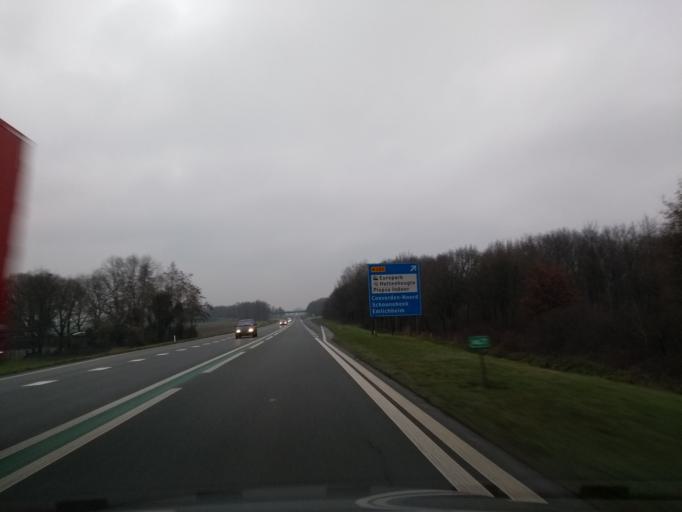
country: NL
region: Drenthe
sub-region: Gemeente Coevorden
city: Coevorden
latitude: 52.6710
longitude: 6.7255
